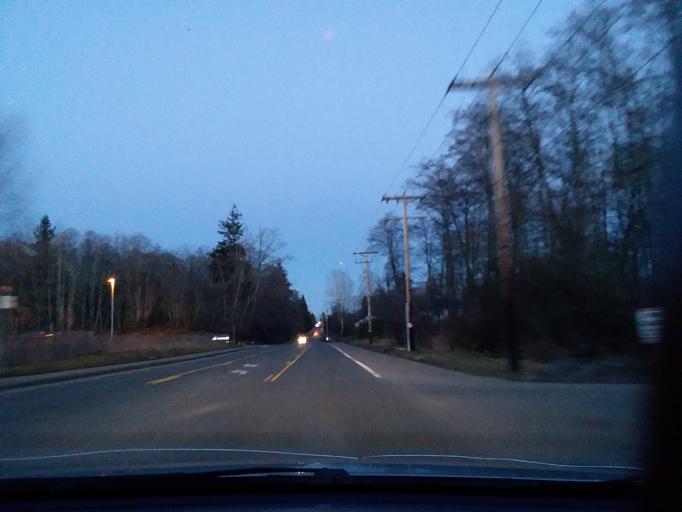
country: US
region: Washington
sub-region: Snohomish County
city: Mukilteo
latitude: 47.9075
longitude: -122.2648
